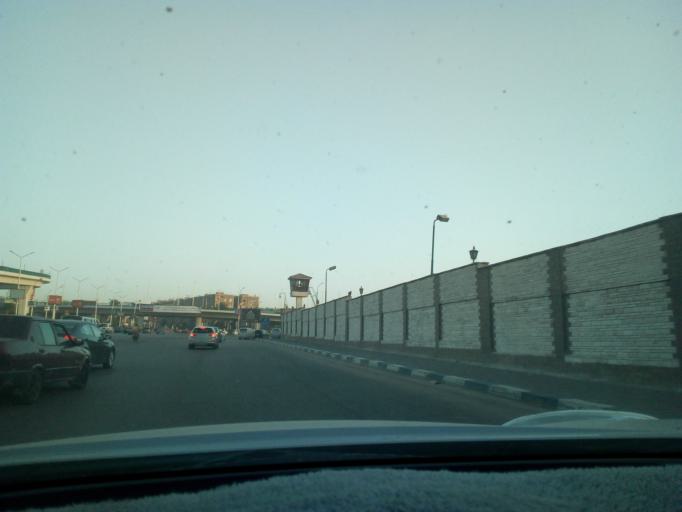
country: EG
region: Muhafazat al Qalyubiyah
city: Al Khankah
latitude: 30.1120
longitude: 31.3687
